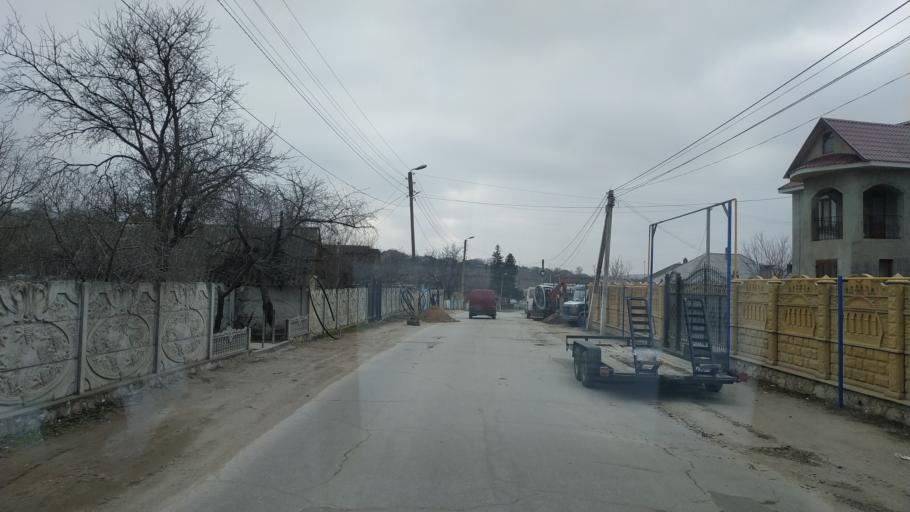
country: MD
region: Hincesti
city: Hincesti
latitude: 46.8803
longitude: 28.4107
